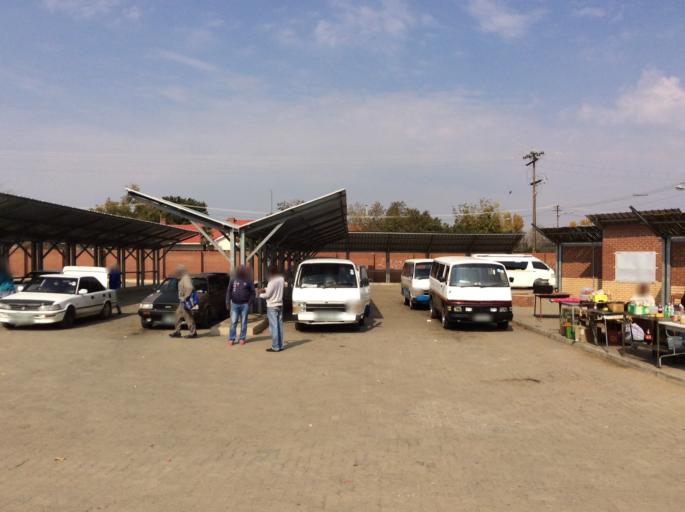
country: LS
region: Mafeteng
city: Mafeteng
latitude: -29.7299
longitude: 27.0371
